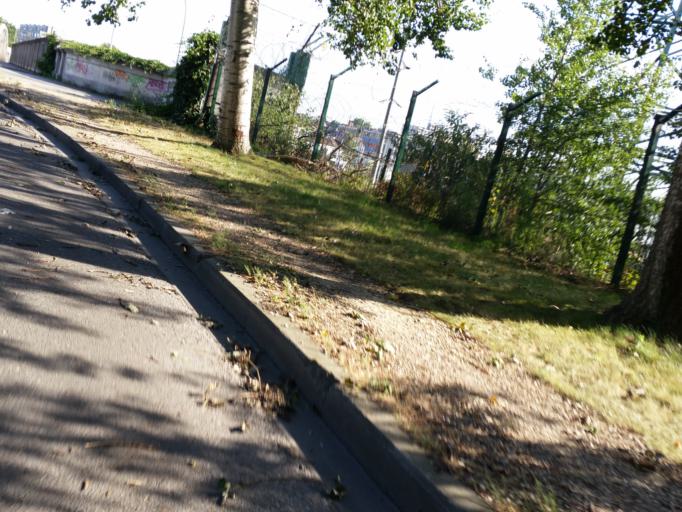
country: BE
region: Brussels Capital
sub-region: Bruxelles-Capitale
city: Brussels
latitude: 50.8818
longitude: 4.3828
